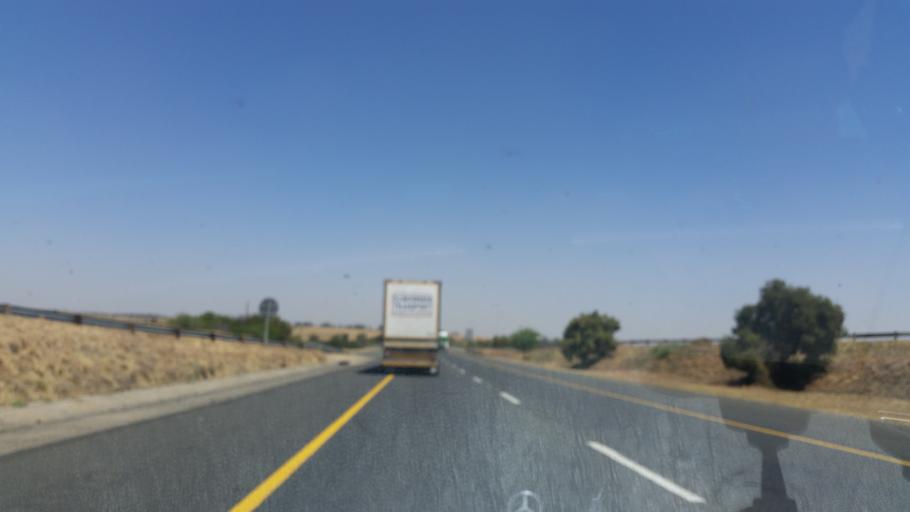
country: ZA
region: Orange Free State
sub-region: Lejweleputswa District Municipality
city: Winburg
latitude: -28.6284
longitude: 26.9083
